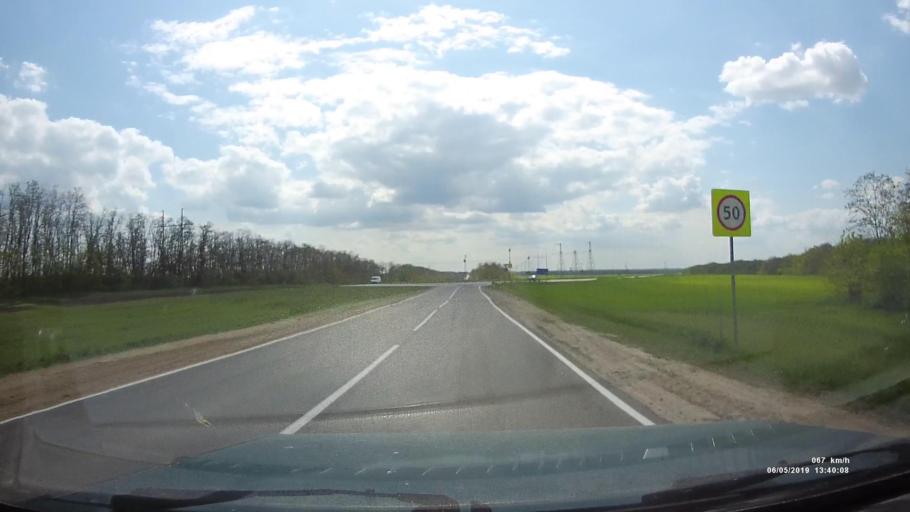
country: RU
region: Rostov
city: Ust'-Donetskiy
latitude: 47.6685
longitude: 40.6968
